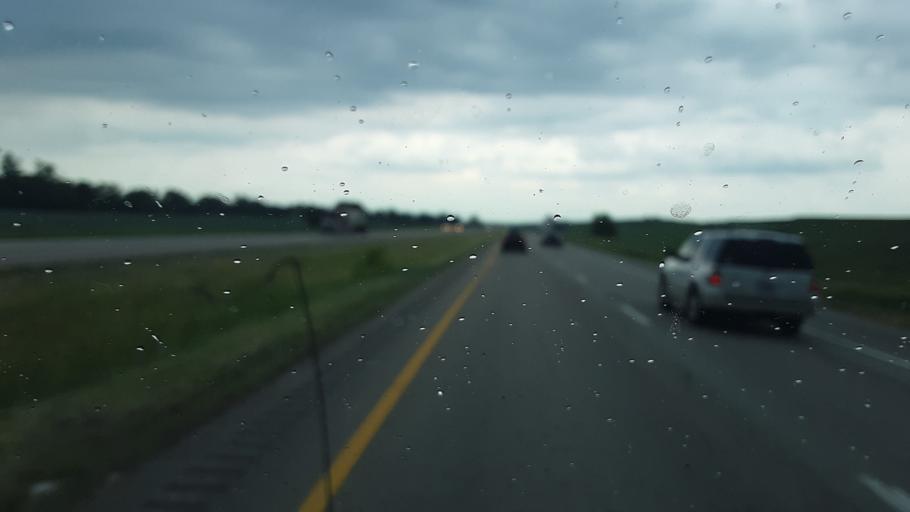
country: US
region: Iowa
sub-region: Pottawattamie County
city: Council Bluffs
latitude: 41.3565
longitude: -95.6956
